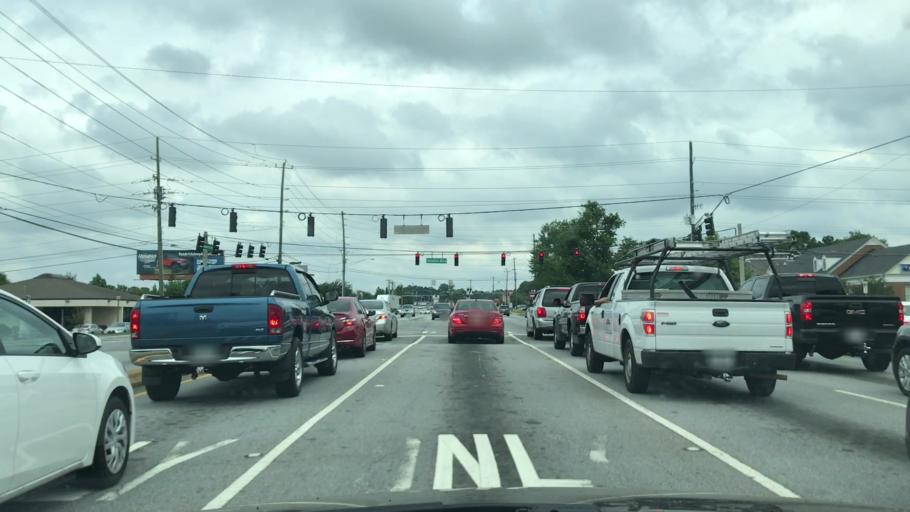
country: US
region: Georgia
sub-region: Gwinnett County
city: Duluth
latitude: 33.9584
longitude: -84.1342
